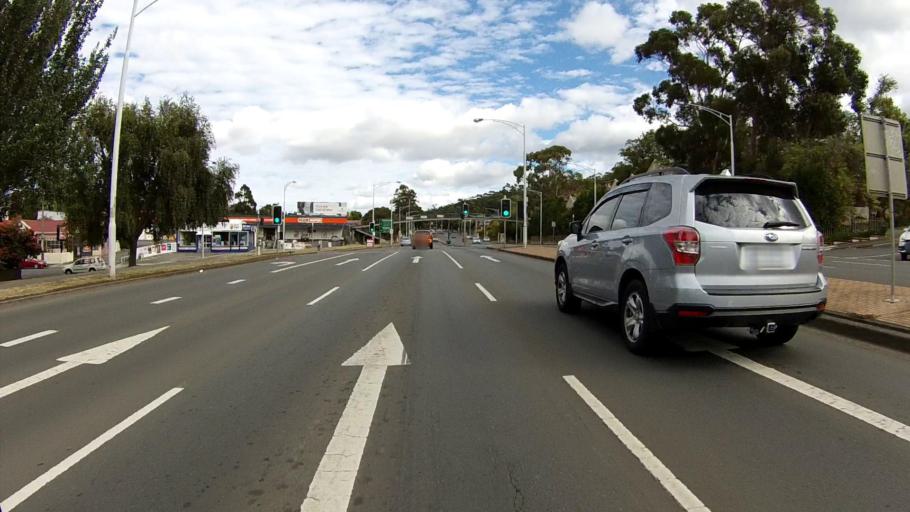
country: AU
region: Tasmania
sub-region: Hobart
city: Hobart
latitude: -42.8741
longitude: 147.3252
